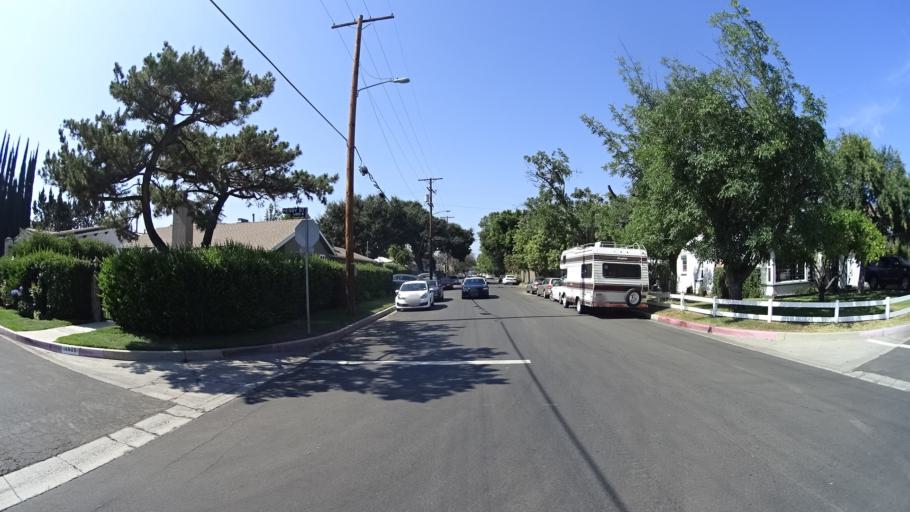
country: US
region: California
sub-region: Los Angeles County
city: Sherman Oaks
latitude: 34.1622
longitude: -118.4553
